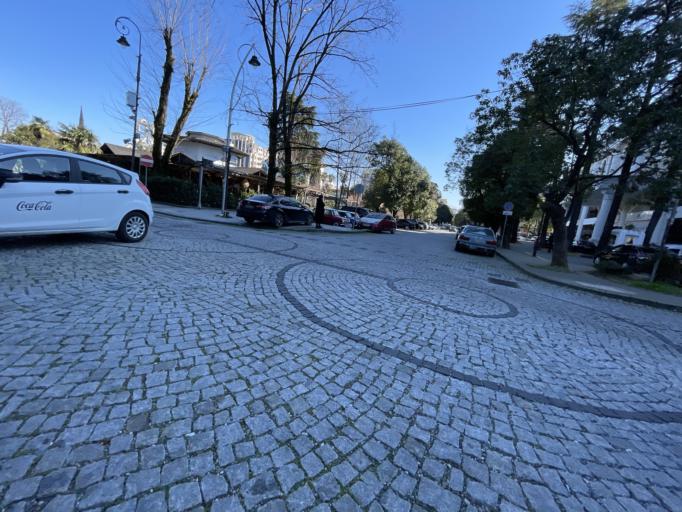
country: GE
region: Ajaria
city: Batumi
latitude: 41.6516
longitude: 41.6308
